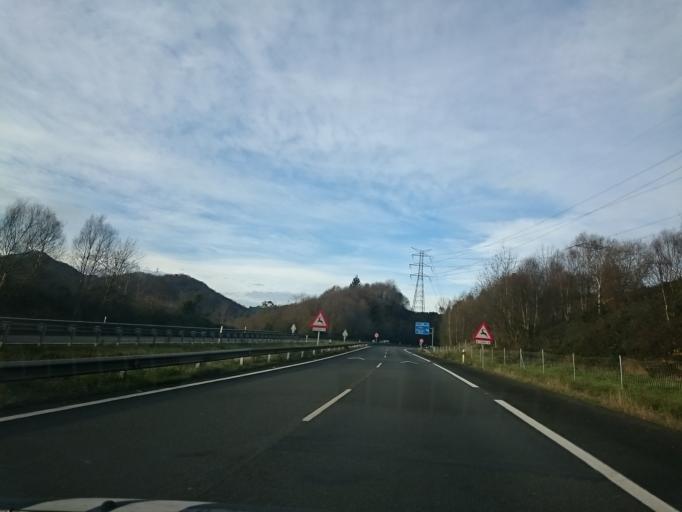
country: ES
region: Asturias
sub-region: Province of Asturias
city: Castandiello
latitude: 43.3103
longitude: -5.8665
